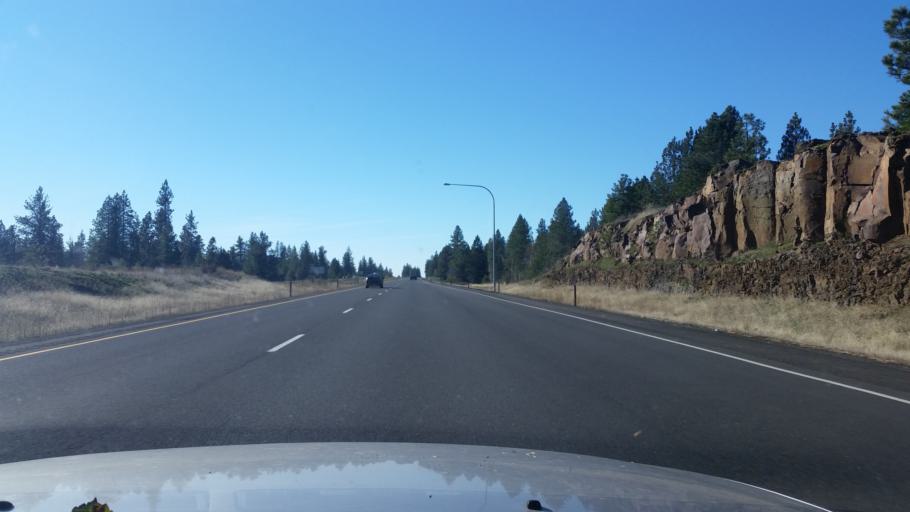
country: US
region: Washington
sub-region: Spokane County
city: Medical Lake
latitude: 47.4330
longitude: -117.7949
